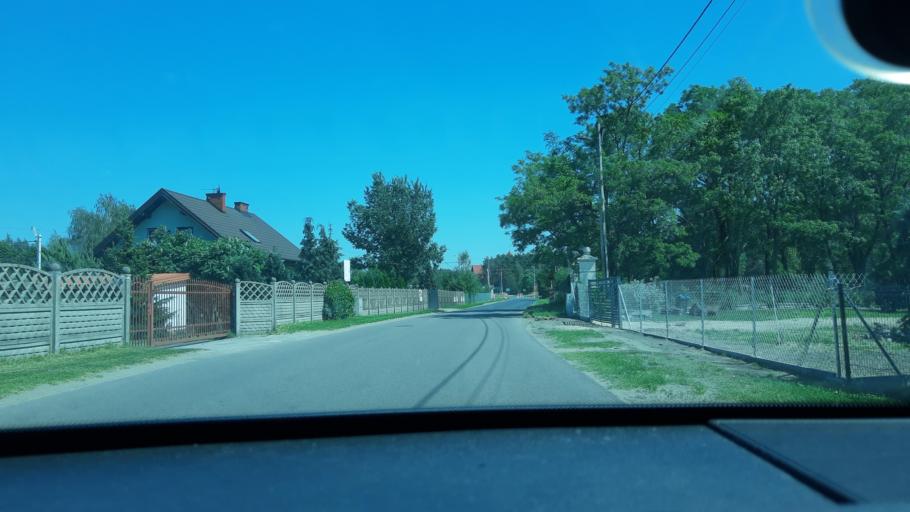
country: PL
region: Lodz Voivodeship
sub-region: Powiat zdunskowolski
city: Zdunska Wola
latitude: 51.6099
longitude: 18.9731
